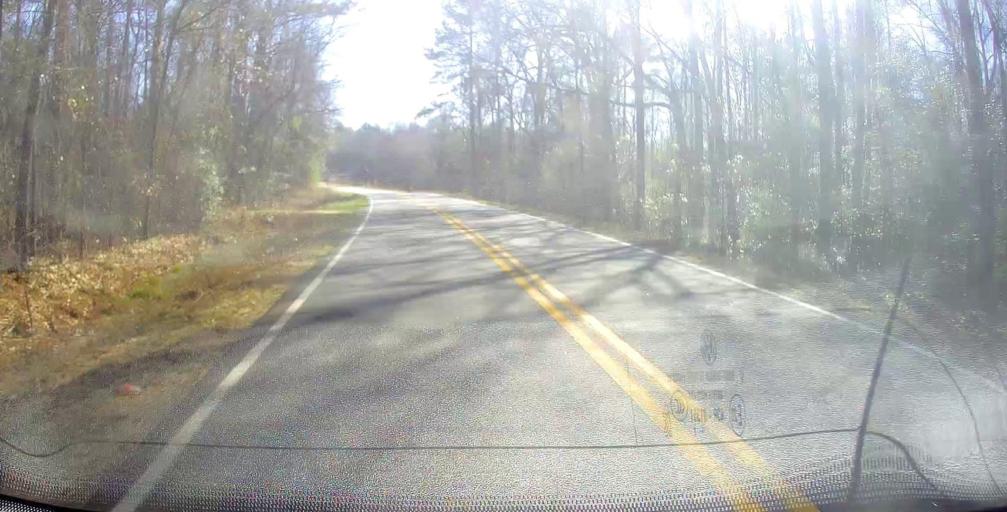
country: US
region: Georgia
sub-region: Crawford County
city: Knoxville
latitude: 32.7093
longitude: -83.9960
